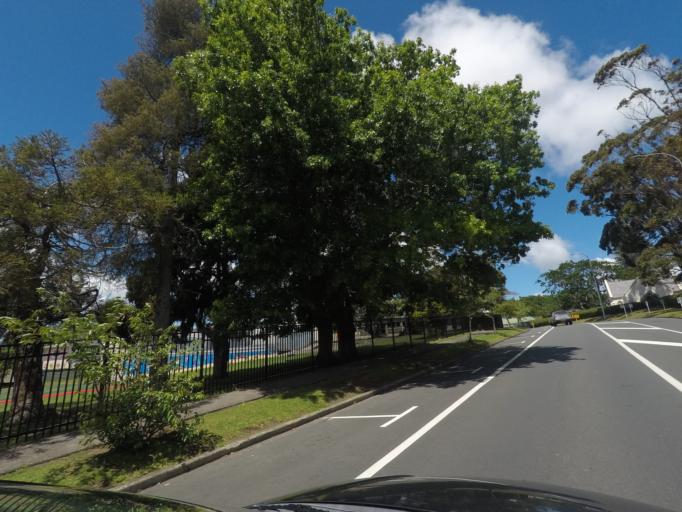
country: NZ
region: Auckland
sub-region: Auckland
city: Waitakere
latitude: -36.9074
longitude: 174.6520
